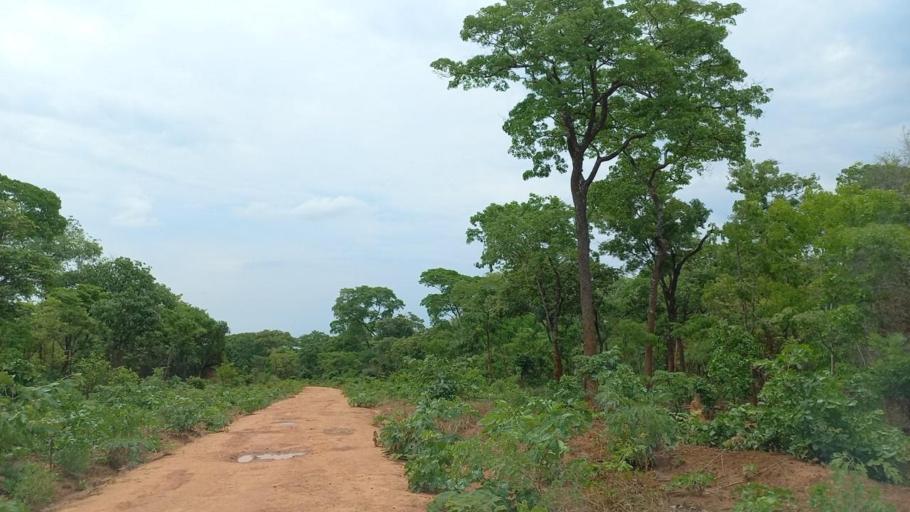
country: ZM
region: North-Western
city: Kalengwa
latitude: -13.6318
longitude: 24.9787
